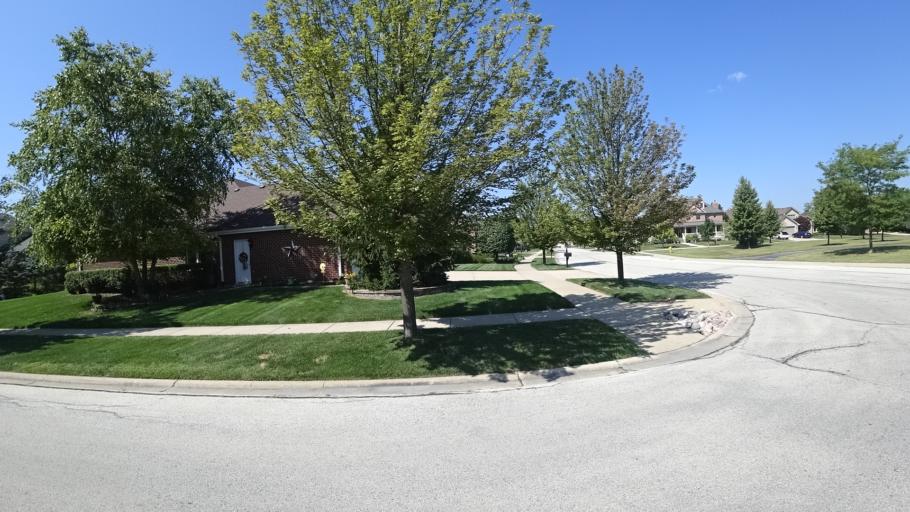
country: US
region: Illinois
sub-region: Cook County
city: Orland Park
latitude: 41.6351
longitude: -87.8317
